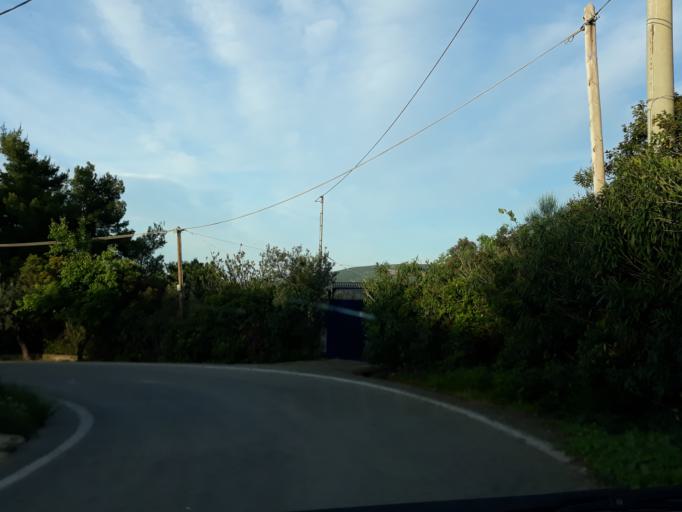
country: GR
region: Attica
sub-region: Nomarchia Anatolikis Attikis
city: Afidnes
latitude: 38.2306
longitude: 23.7874
